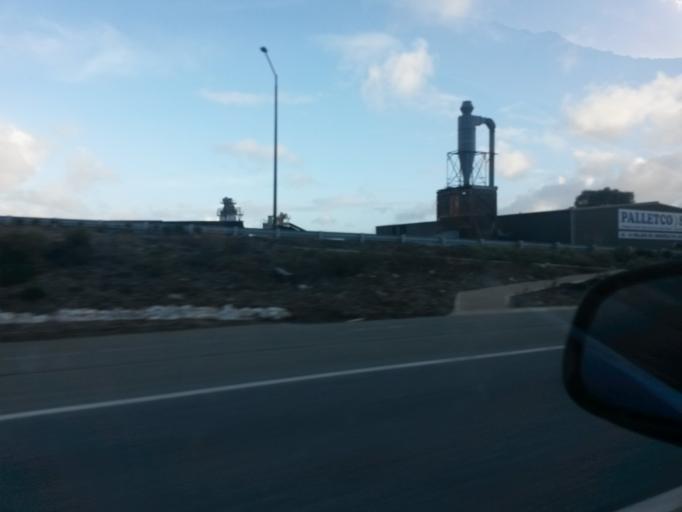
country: AU
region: South Australia
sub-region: Charles Sturt
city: Woodville North
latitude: -34.8330
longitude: 138.5614
